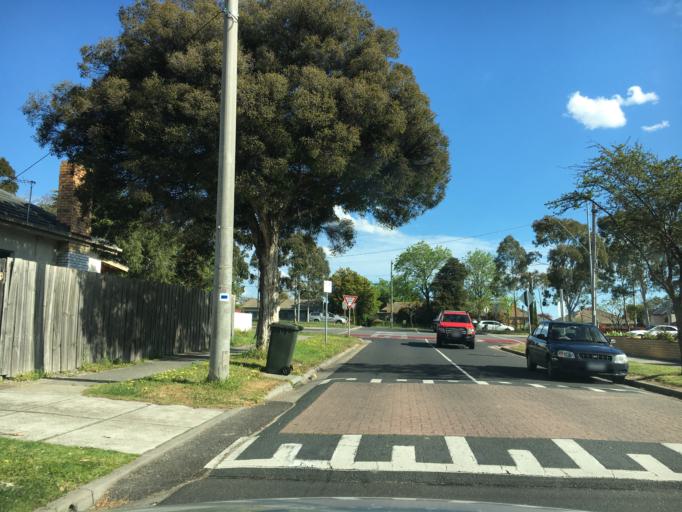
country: AU
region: Victoria
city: Clayton
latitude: -37.9128
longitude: 145.1186
